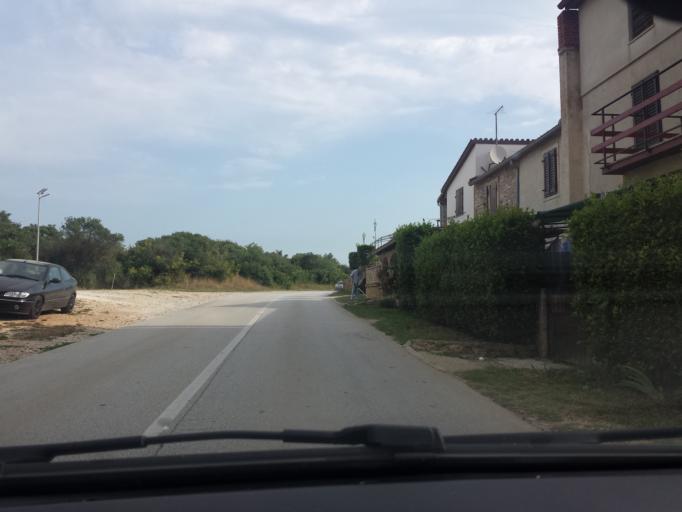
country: HR
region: Istarska
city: Galizana
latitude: 44.9084
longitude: 13.8556
